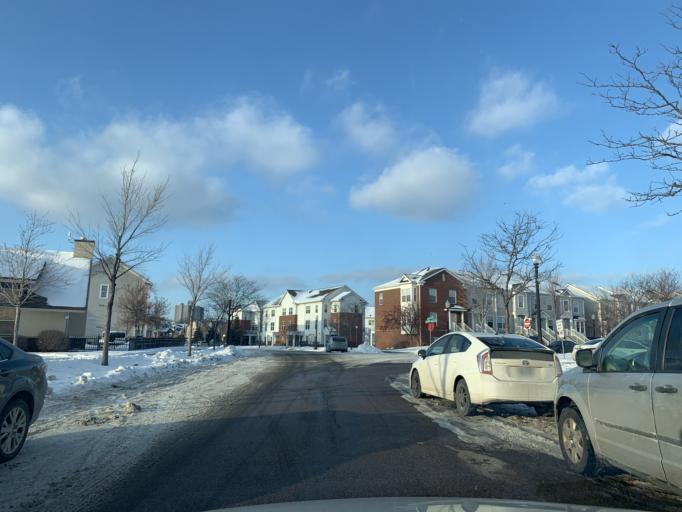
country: US
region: Minnesota
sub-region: Hennepin County
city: Minneapolis
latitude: 44.9848
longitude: -93.2913
